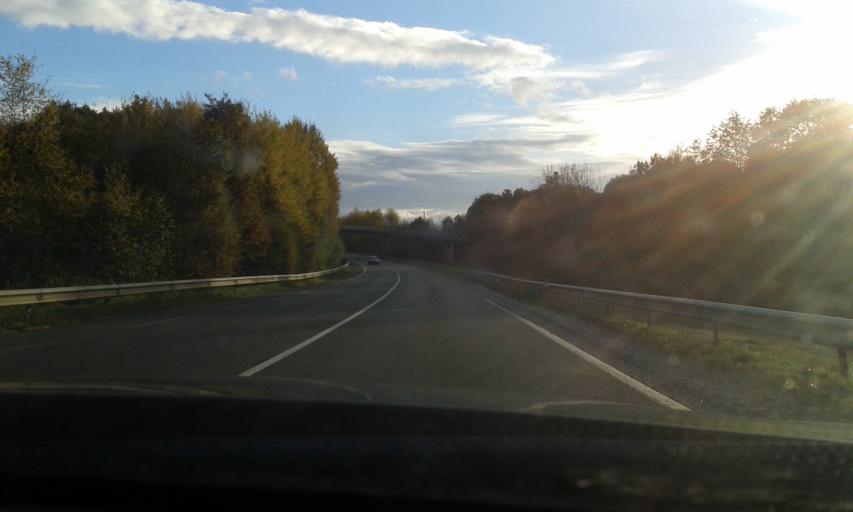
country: FR
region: Centre
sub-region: Departement d'Eure-et-Loir
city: Leves
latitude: 48.4800
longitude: 1.4612
